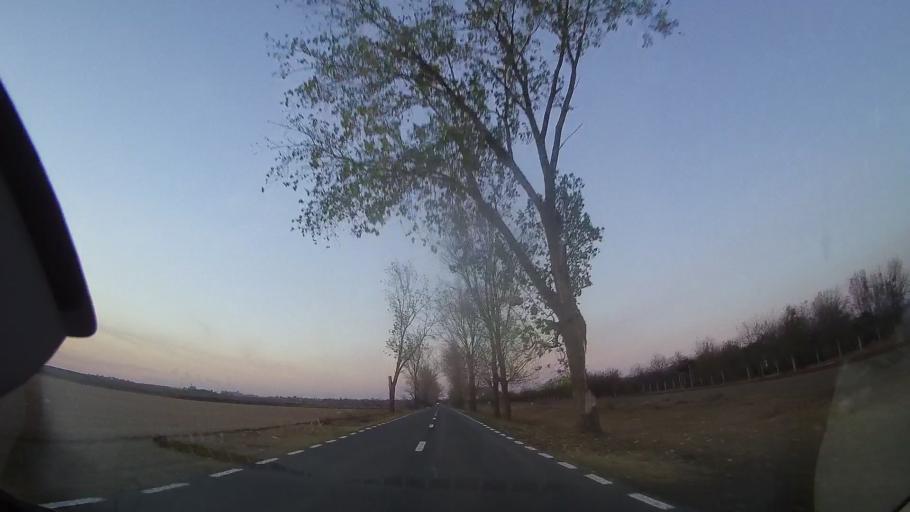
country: RO
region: Constanta
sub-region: Comuna Cobadin
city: Cobadin
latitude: 44.0442
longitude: 28.2540
